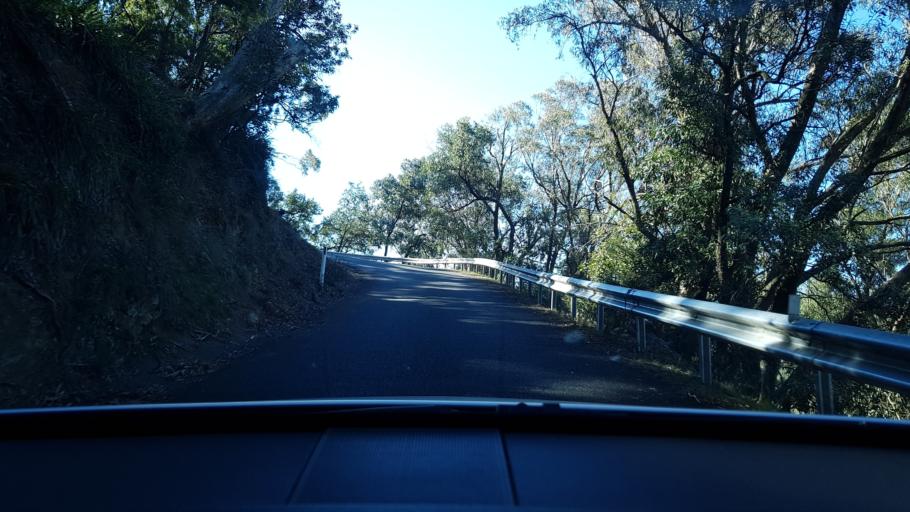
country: AU
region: New South Wales
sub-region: Oberon
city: Oberon
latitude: -33.8153
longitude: 150.0179
